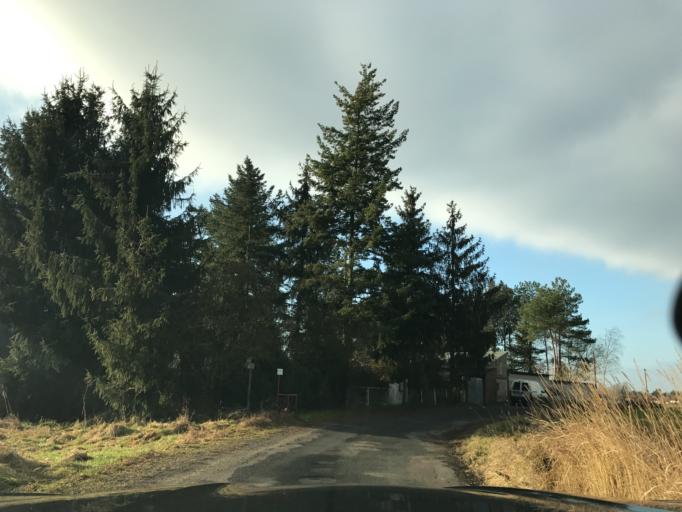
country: DE
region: Brandenburg
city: Brandenburg an der Havel
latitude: 52.3671
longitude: 12.5377
